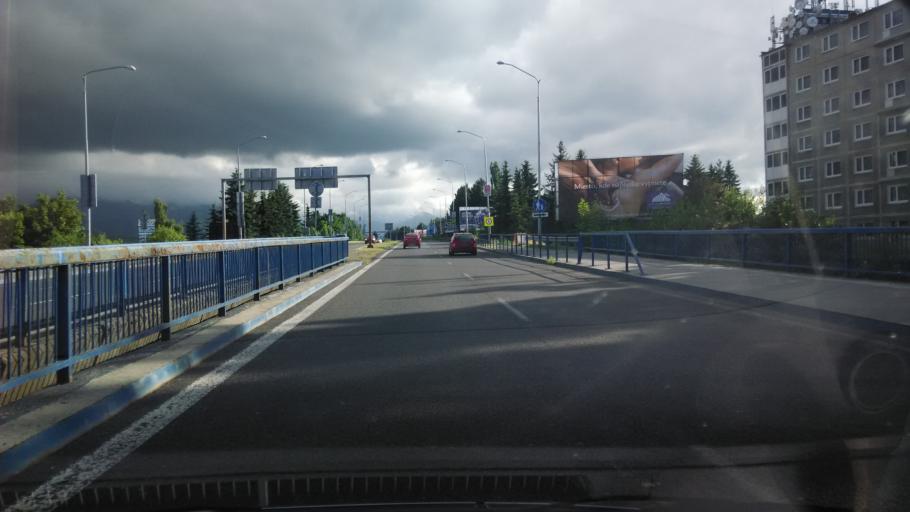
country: SK
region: Zilinsky
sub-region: Okres Liptovsky Mikulas
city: Liptovsky Mikulas
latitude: 49.0828
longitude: 19.6055
